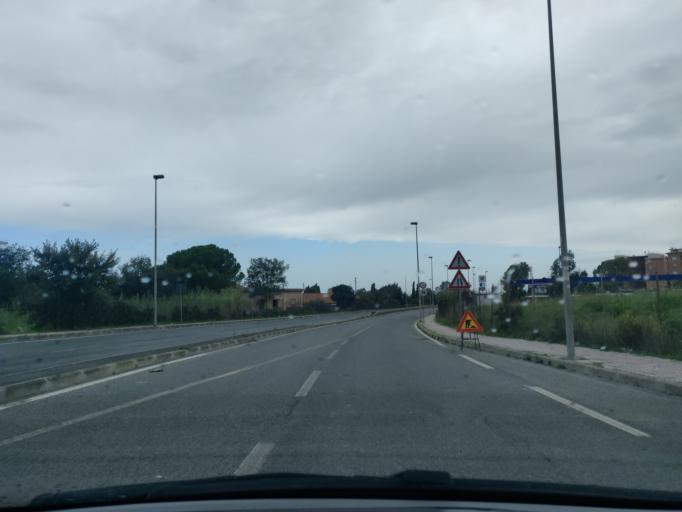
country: IT
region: Latium
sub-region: Citta metropolitana di Roma Capitale
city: Civitavecchia
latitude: 42.0997
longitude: 11.7972
